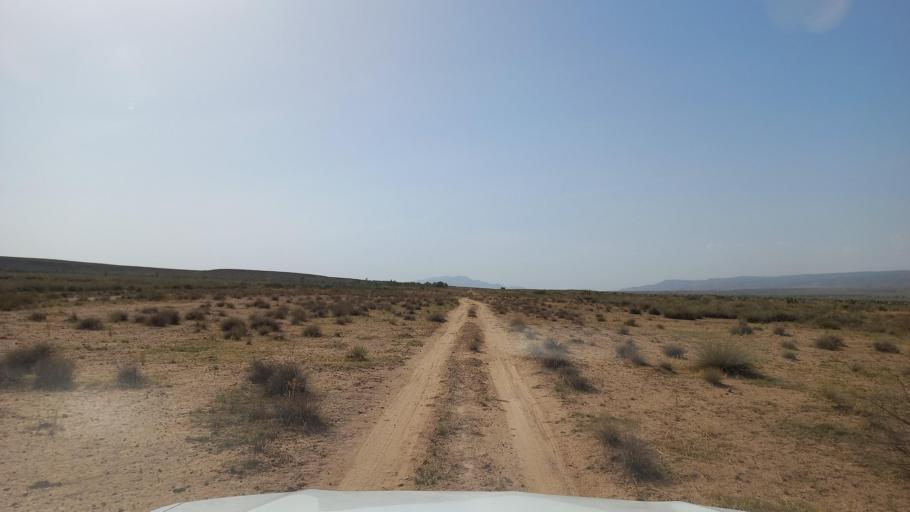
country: TN
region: Al Qasrayn
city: Kasserine
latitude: 35.2141
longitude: 9.0054
